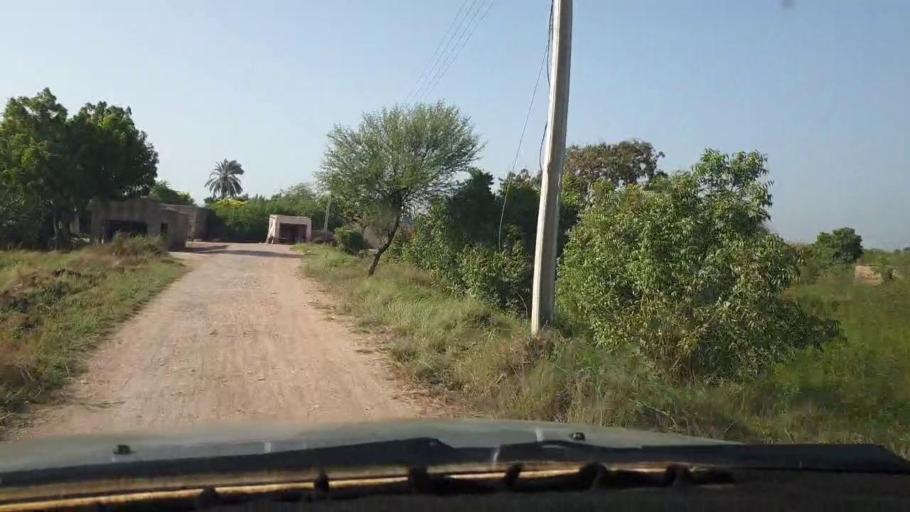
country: PK
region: Sindh
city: Chambar
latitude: 25.2703
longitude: 68.9233
